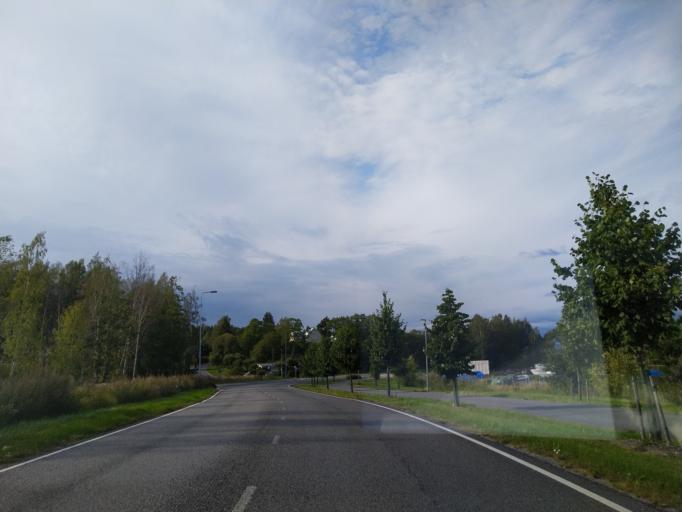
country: FI
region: Varsinais-Suomi
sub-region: Turku
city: Turku
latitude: 60.4229
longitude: 22.2276
